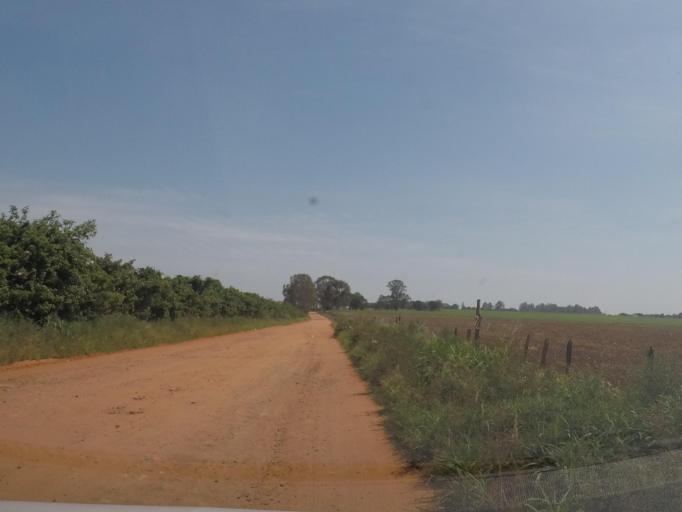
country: BR
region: Sao Paulo
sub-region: Sumare
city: Sumare
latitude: -22.8709
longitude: -47.2868
